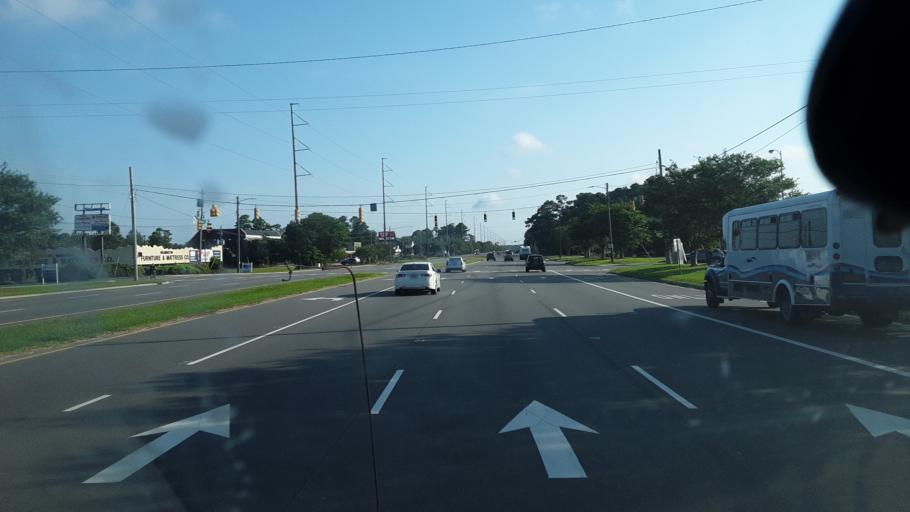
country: US
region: North Carolina
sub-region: New Hanover County
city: Seagate
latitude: 34.2201
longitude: -77.8842
